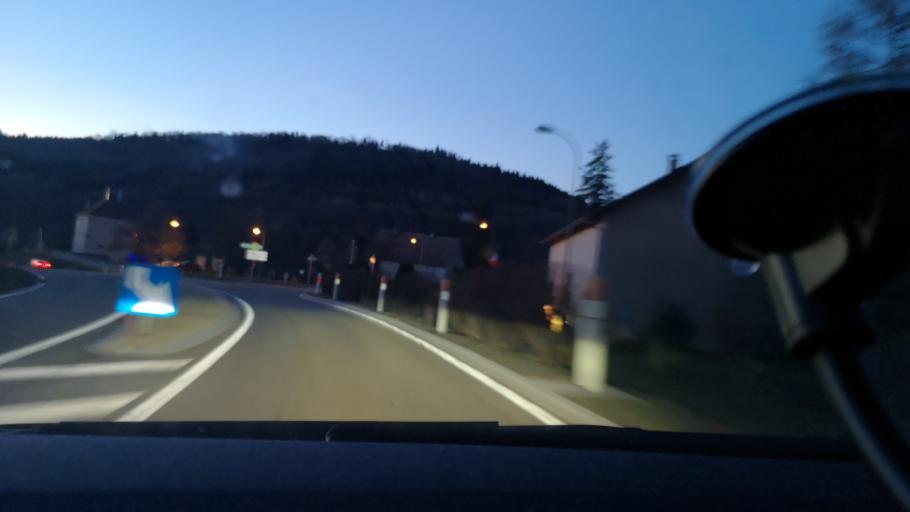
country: FR
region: Franche-Comte
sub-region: Departement du Jura
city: Champagnole
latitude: 46.7585
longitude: 5.9412
